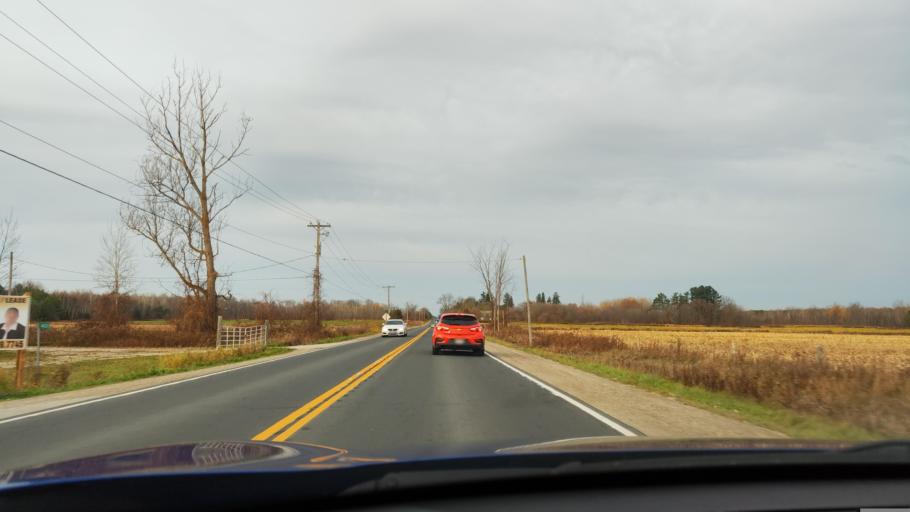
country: CA
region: Ontario
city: Angus
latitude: 44.3644
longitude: -79.9443
